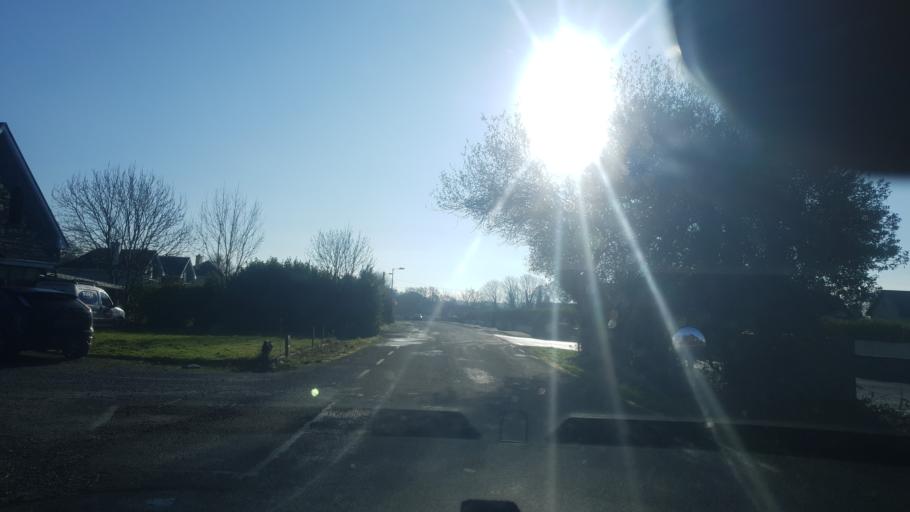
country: IE
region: Munster
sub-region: Ciarrai
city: Cill Airne
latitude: 52.1005
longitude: -9.4716
